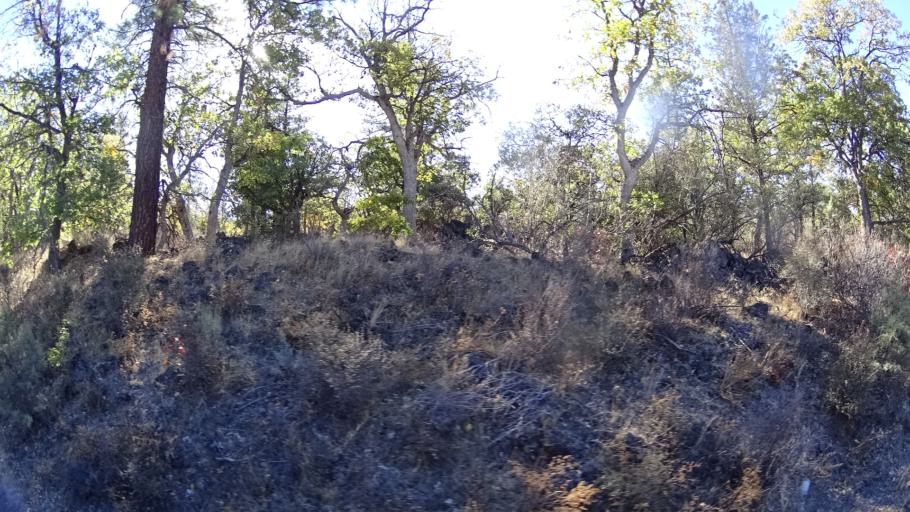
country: US
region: California
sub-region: Siskiyou County
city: Montague
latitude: 41.9862
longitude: -122.3566
